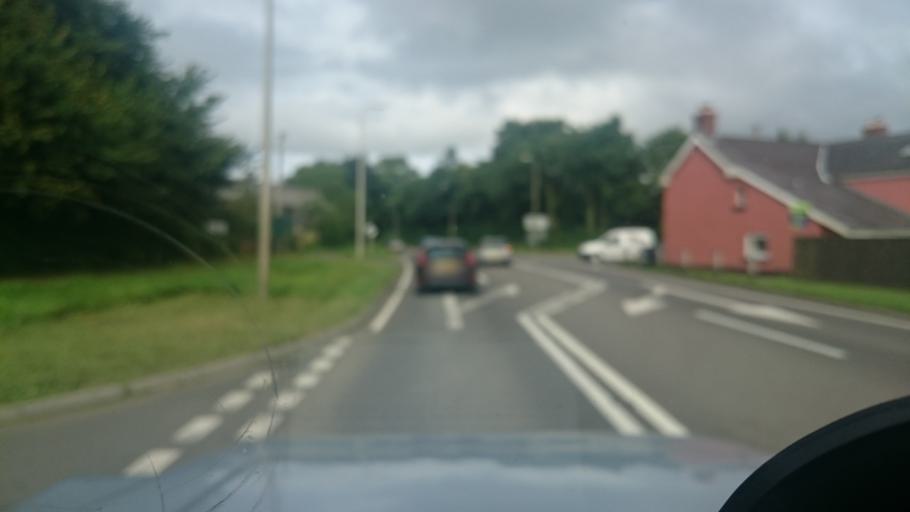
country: GB
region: Wales
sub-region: Pembrokeshire
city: Narberth
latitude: 51.8119
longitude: -4.7458
